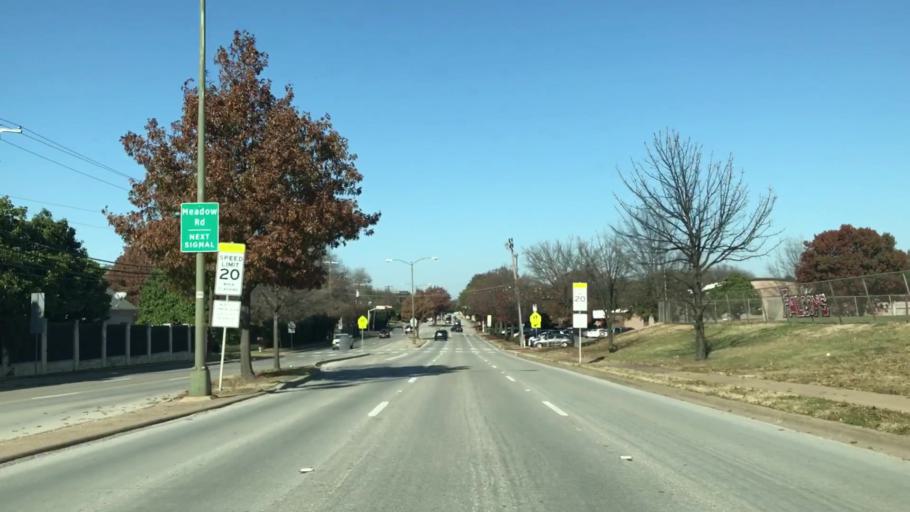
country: US
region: Texas
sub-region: Dallas County
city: University Park
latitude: 32.8845
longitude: -96.7867
